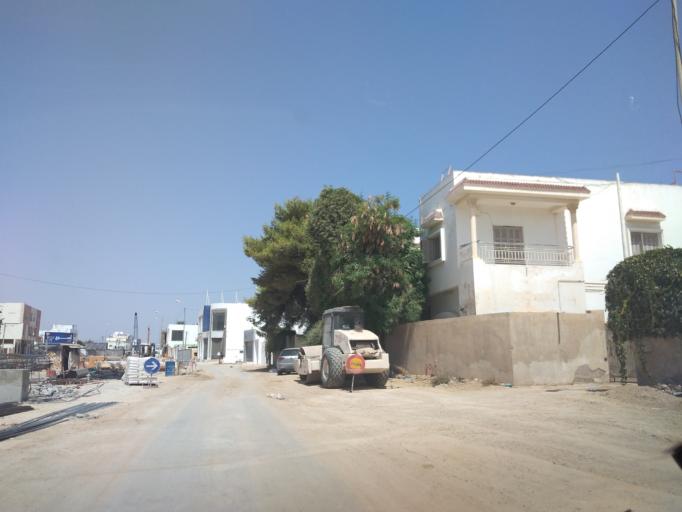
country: TN
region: Safaqis
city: Sfax
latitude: 34.7499
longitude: 10.7292
